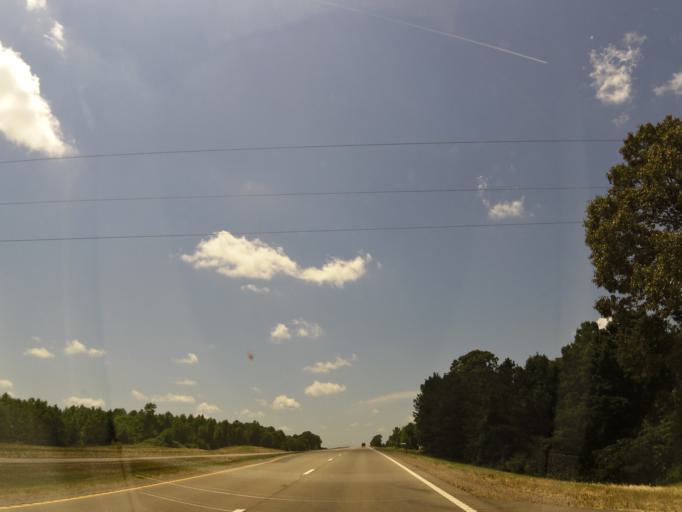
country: US
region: Mississippi
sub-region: Pontotoc County
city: Pontotoc
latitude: 34.2913
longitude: -89.1943
